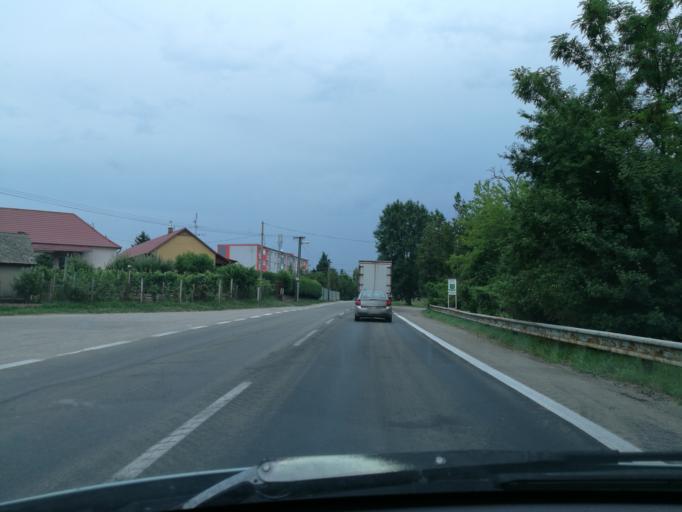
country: SK
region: Nitriansky
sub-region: Okres Komarno
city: Hurbanovo
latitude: 47.9308
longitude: 18.2064
